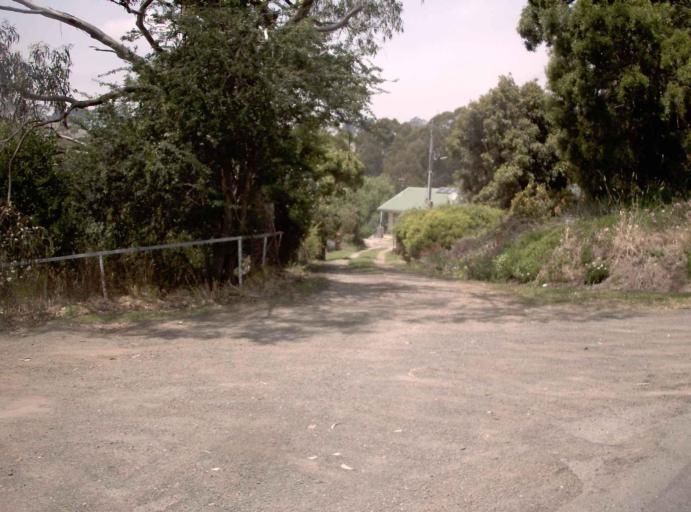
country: AU
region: Victoria
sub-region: Latrobe
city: Traralgon
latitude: -38.3276
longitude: 146.7238
